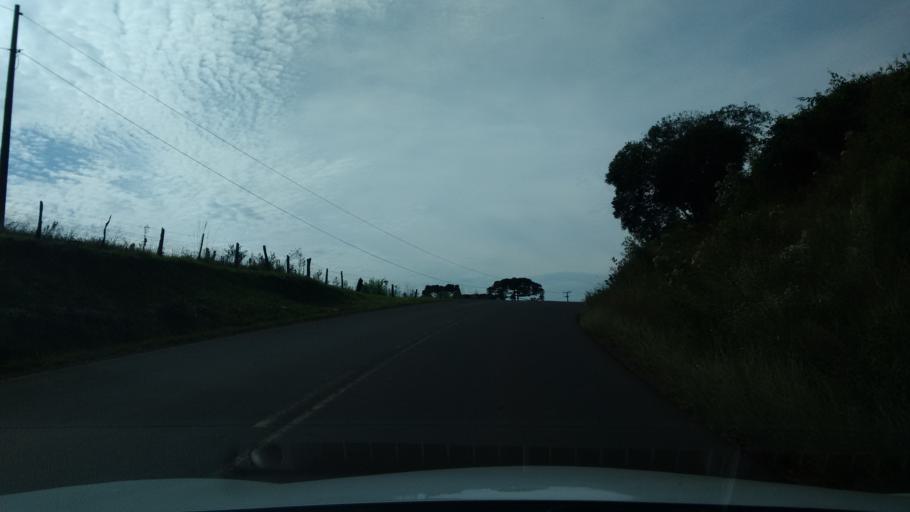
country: BR
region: Santa Catarina
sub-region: Videira
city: Videira
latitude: -27.2396
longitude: -50.9786
